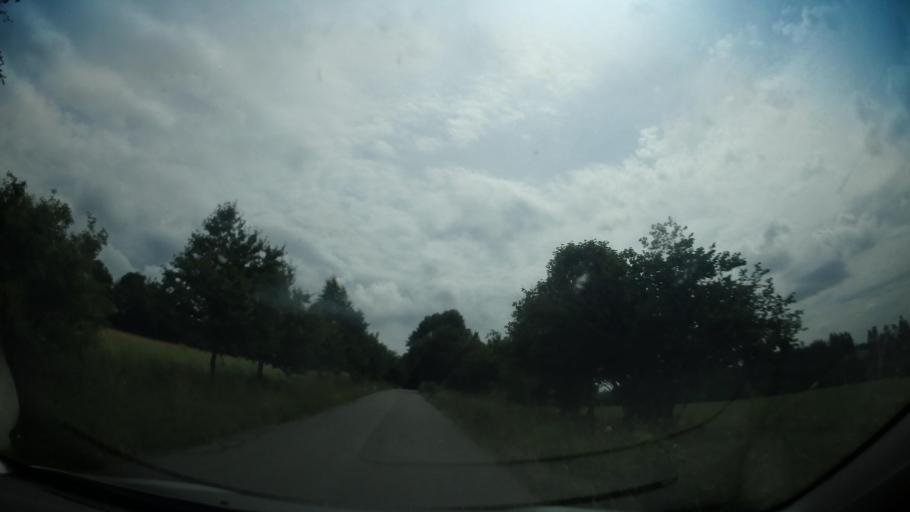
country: CZ
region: Vysocina
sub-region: Okres Zd'ar nad Sazavou
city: Nove Mesto na Morave
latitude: 49.6003
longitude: 16.0589
